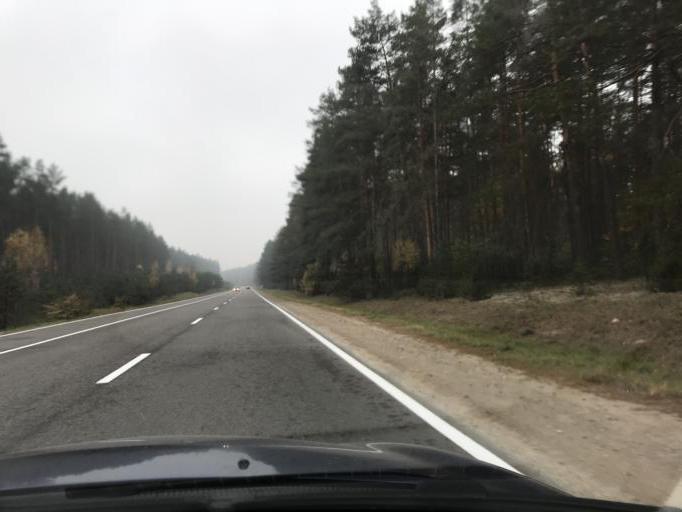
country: LT
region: Alytaus apskritis
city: Druskininkai
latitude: 53.9236
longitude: 23.9310
